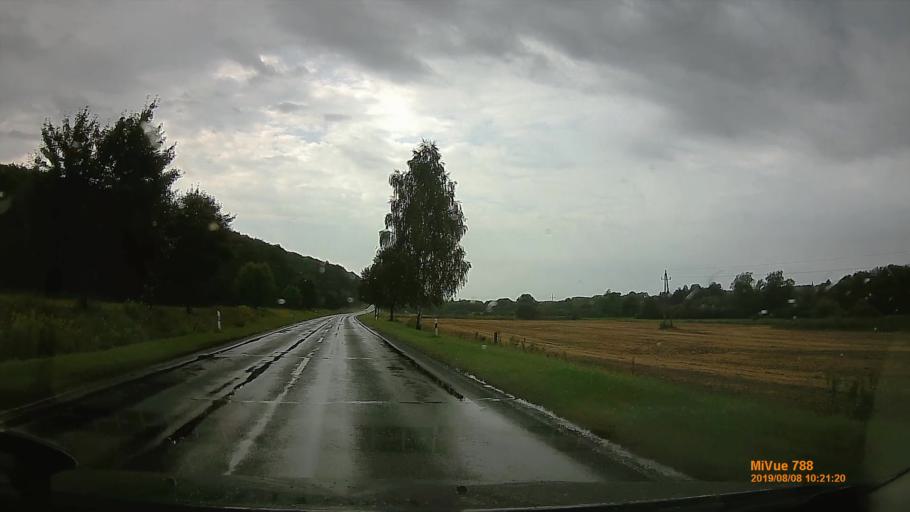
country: HU
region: Zala
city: Zalaegerszeg
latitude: 46.7400
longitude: 16.8557
